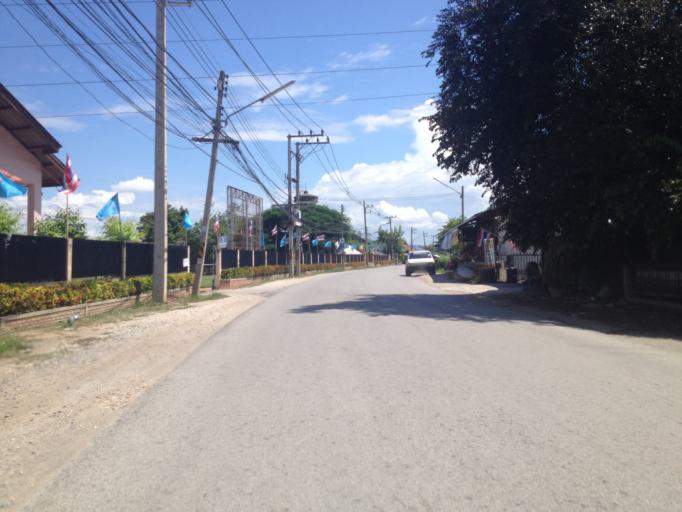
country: TH
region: Chiang Mai
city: San Pa Tong
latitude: 18.6444
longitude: 98.9272
